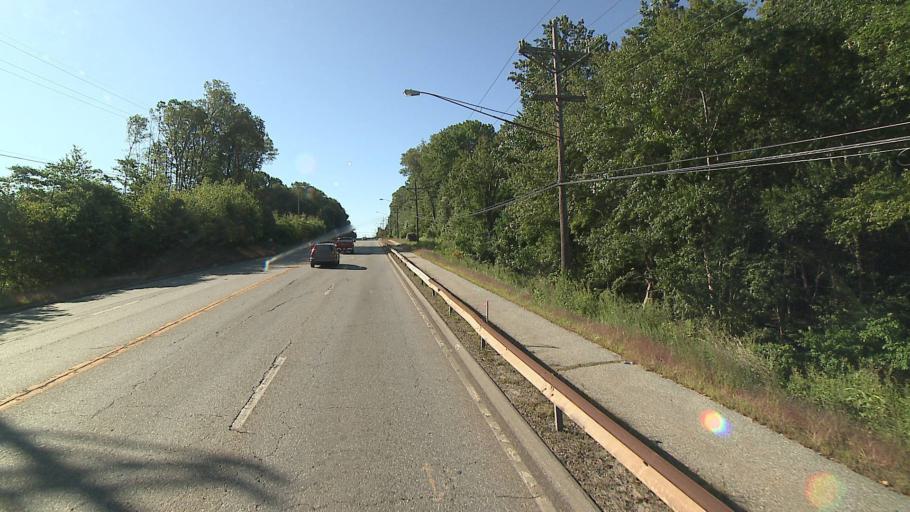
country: US
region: Connecticut
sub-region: New London County
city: Conning Towers-Nautilus Park
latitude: 41.3855
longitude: -72.0783
